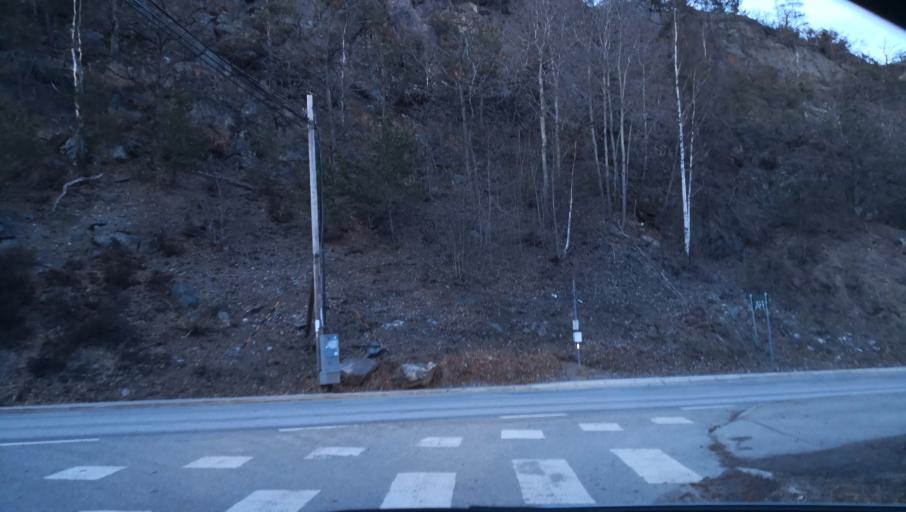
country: SE
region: Stockholm
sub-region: Varmdo Kommun
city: Gustavsberg
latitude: 59.3275
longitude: 18.3561
